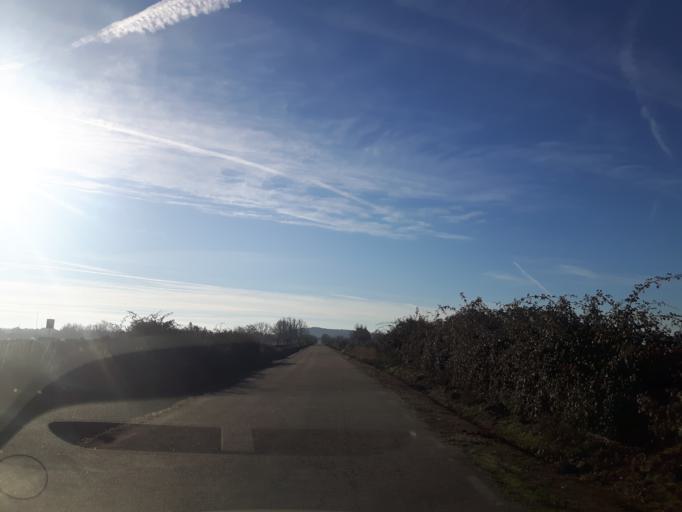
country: ES
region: Castille and Leon
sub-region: Provincia de Salamanca
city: Cerralbo
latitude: 40.9321
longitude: -6.6191
